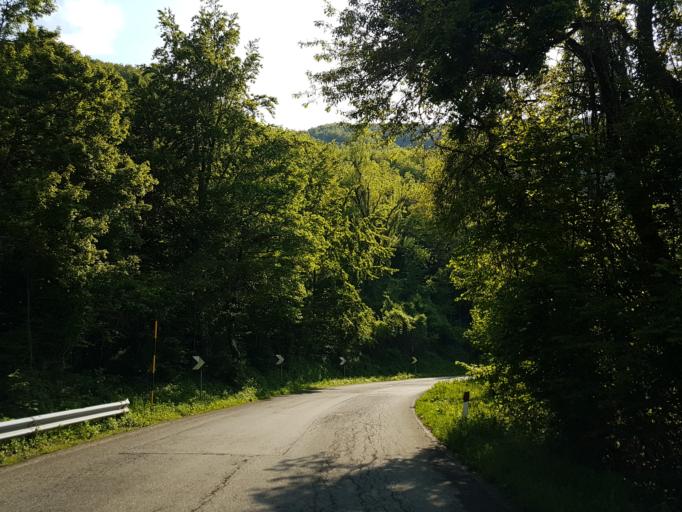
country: IT
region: Emilia-Romagna
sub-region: Forli-Cesena
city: San Piero in Bagno
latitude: 43.8118
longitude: 11.9203
